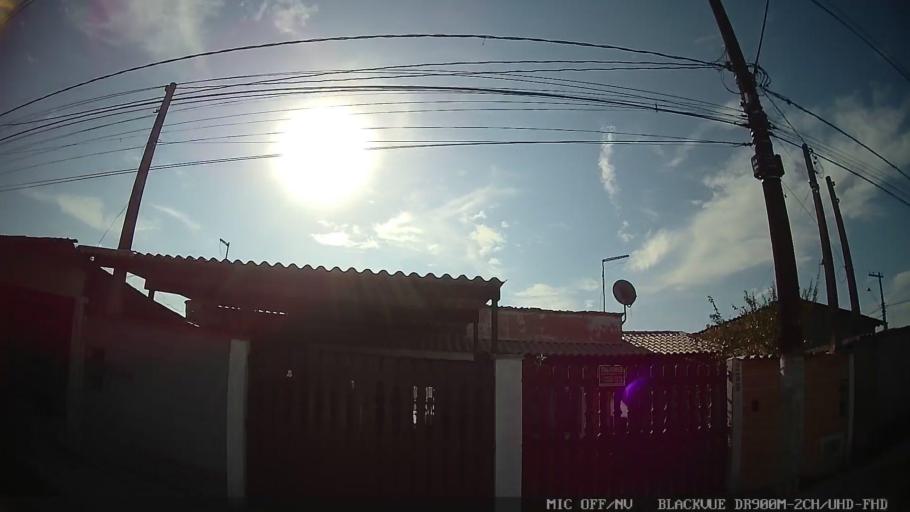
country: BR
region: Sao Paulo
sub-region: Itanhaem
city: Itanhaem
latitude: -24.1794
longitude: -46.8178
